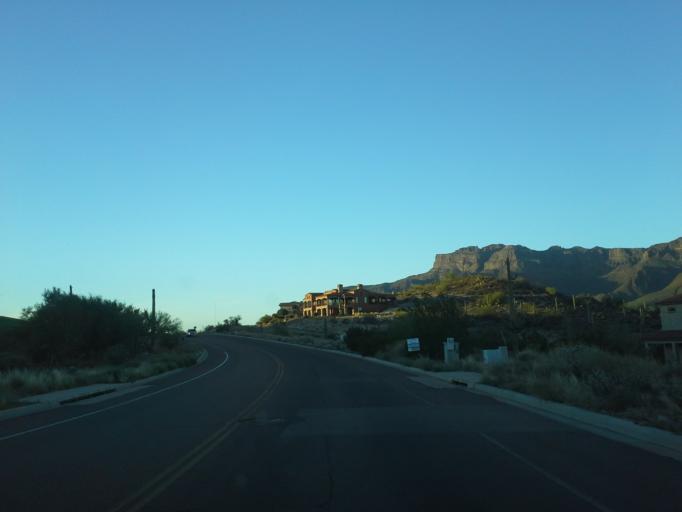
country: US
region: Arizona
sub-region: Pinal County
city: Apache Junction
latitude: 33.3788
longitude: -111.4433
